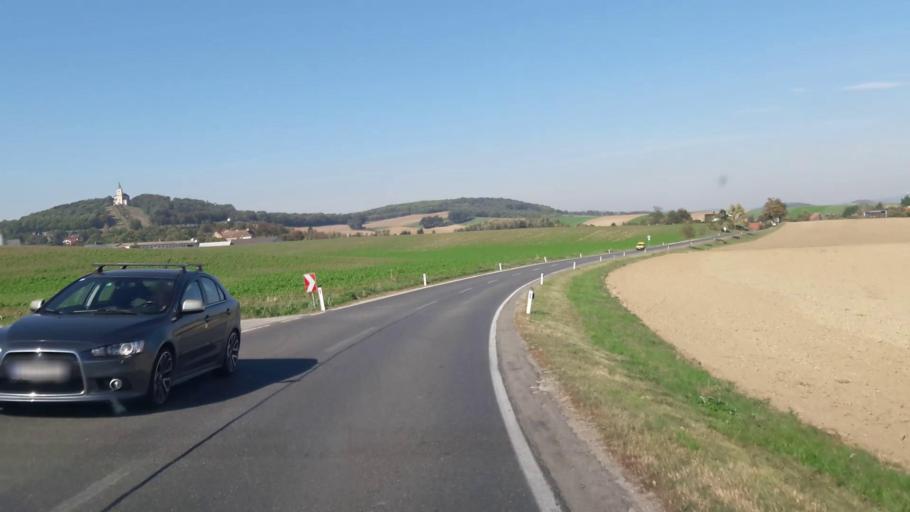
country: AT
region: Lower Austria
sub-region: Politischer Bezirk Korneuburg
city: Grossrussbach
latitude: 48.4542
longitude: 16.3735
